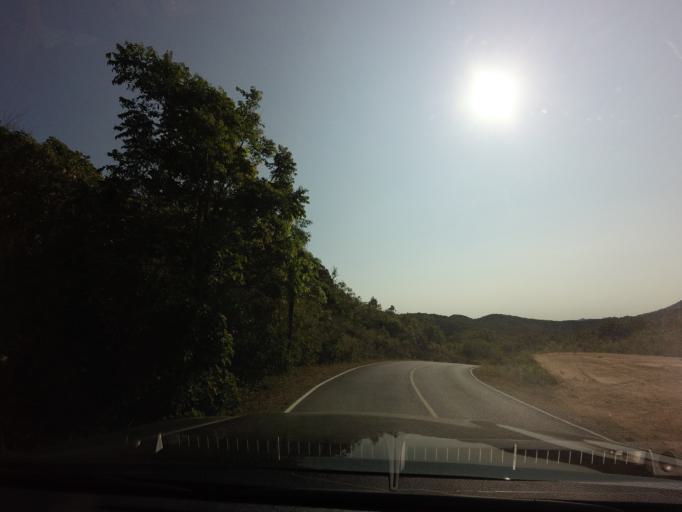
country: TH
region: Kanchanaburi
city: Thong Pha Phum
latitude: 14.6768
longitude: 98.3741
